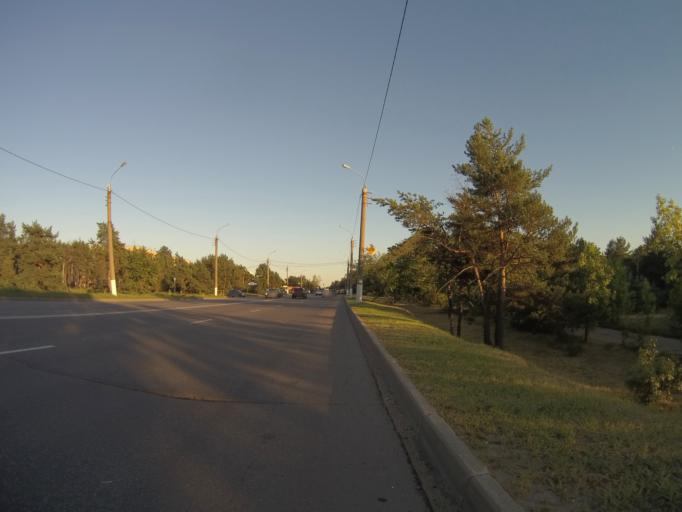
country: RU
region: Vladimir
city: Kommunar
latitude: 56.1046
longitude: 40.4357
